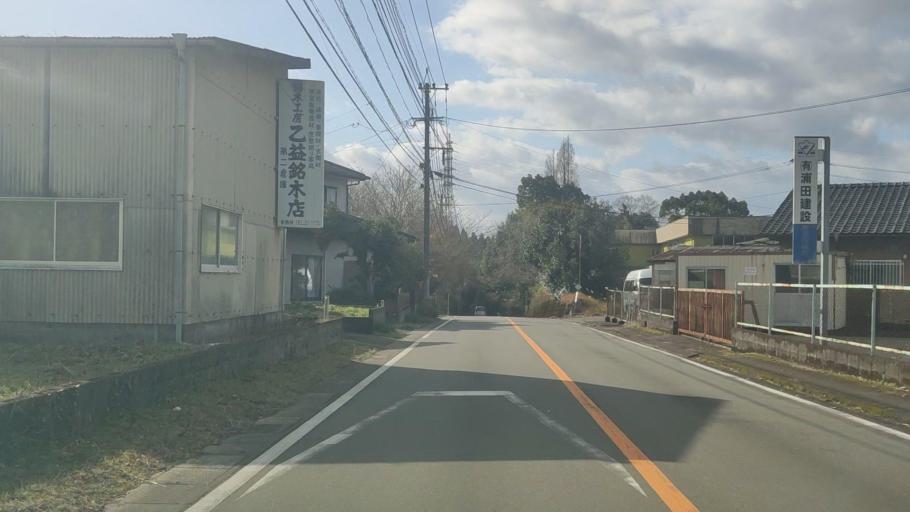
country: JP
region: Kumamoto
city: Hitoyoshi
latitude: 32.2279
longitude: 130.7822
